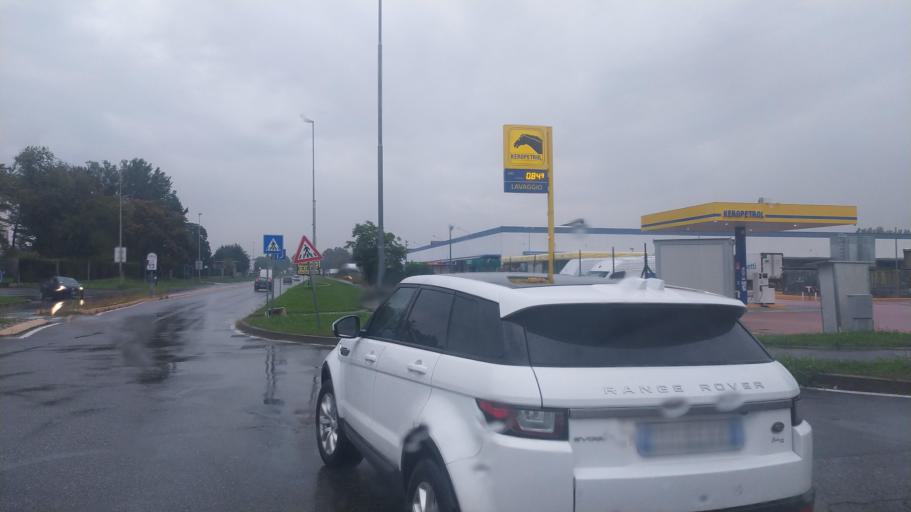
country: IT
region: Lombardy
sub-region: Citta metropolitana di Milano
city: Cusago
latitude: 45.4403
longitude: 9.0436
